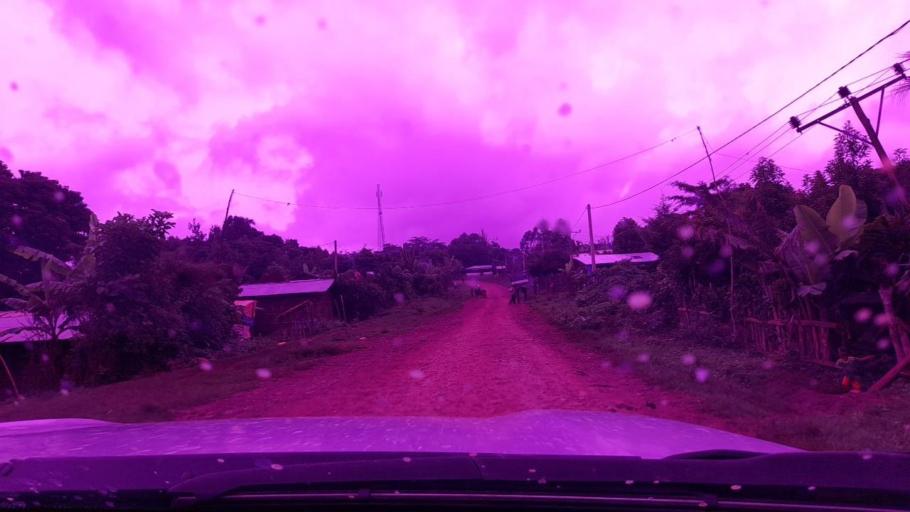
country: ET
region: Southern Nations, Nationalities, and People's Region
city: Bonga
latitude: 7.5525
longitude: 35.8608
